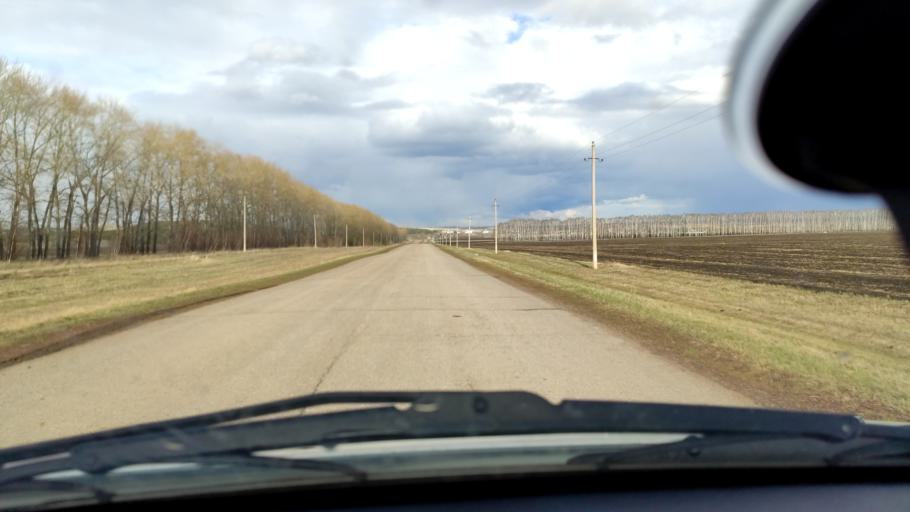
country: RU
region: Bashkortostan
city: Buzdyak
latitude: 54.7610
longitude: 54.5726
